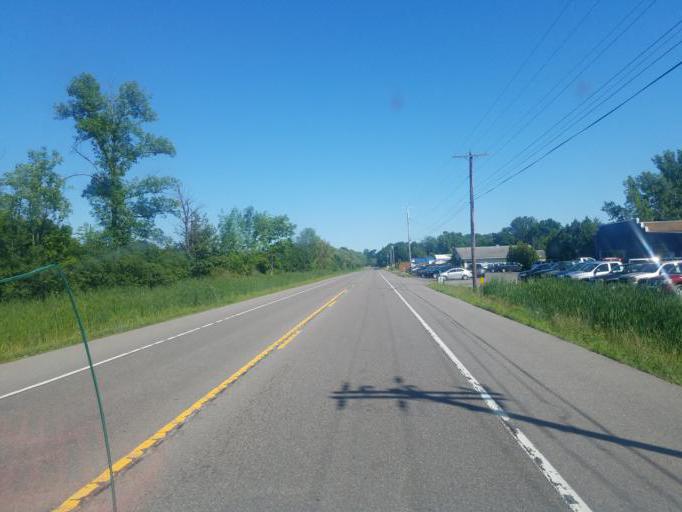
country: US
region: New York
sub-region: Wayne County
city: Lyons
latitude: 43.0640
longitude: -77.0243
